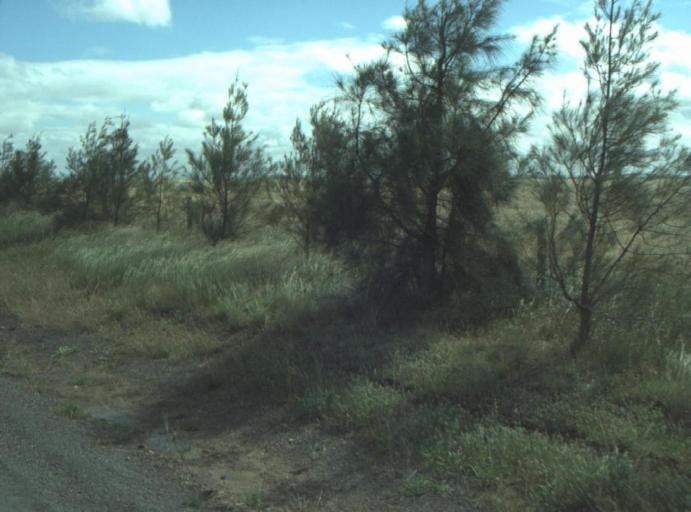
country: AU
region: Victoria
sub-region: Greater Geelong
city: Lara
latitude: -37.8905
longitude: 144.3194
